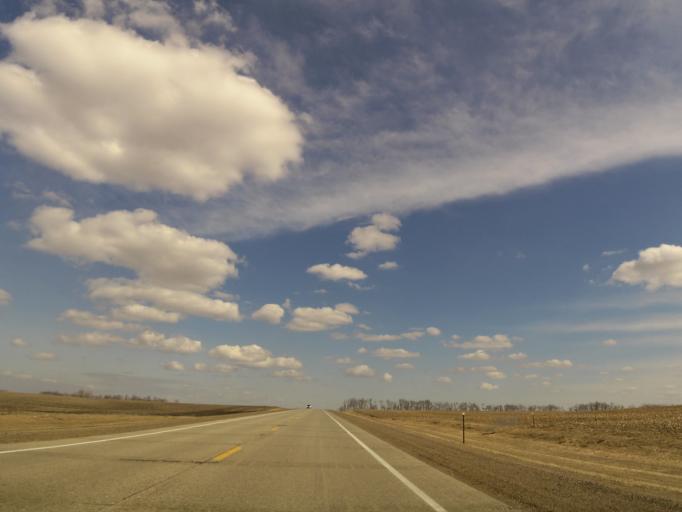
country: US
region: South Dakota
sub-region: Deuel County
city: Clear Lake
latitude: 44.8900
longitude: -96.8107
